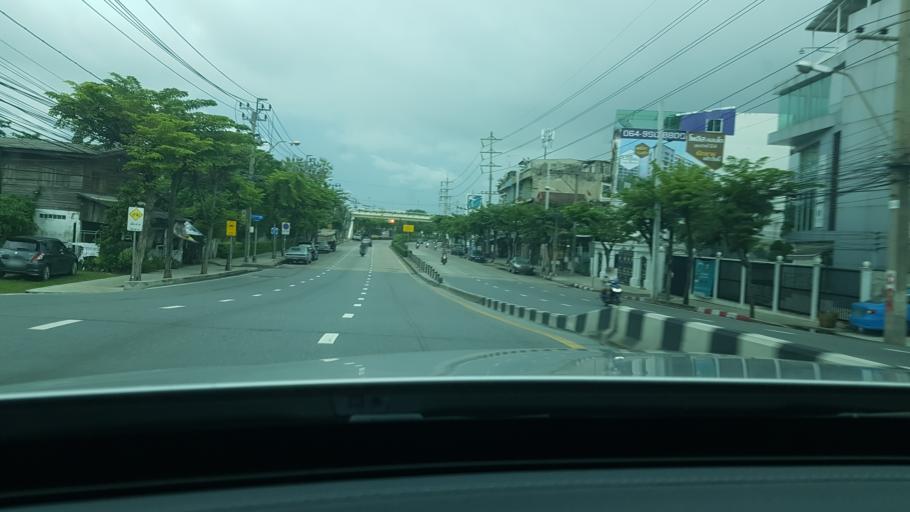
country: TH
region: Bangkok
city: Rat Burana
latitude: 13.6747
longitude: 100.5175
